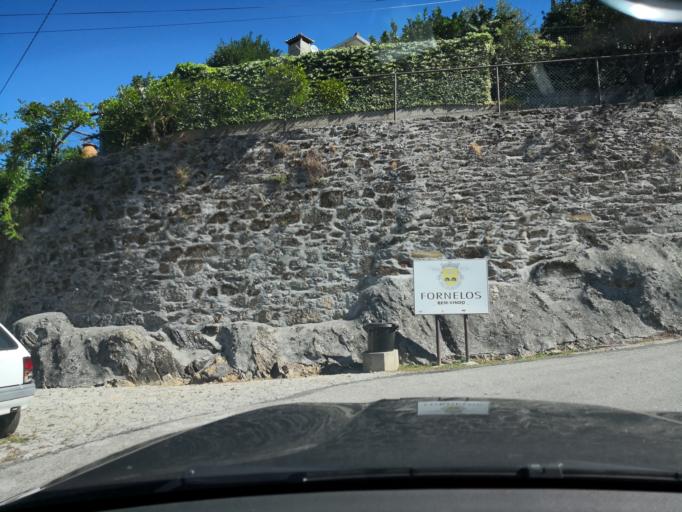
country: PT
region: Vila Real
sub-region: Santa Marta de Penaguiao
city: Santa Marta de Penaguiao
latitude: 41.2479
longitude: -7.8081
